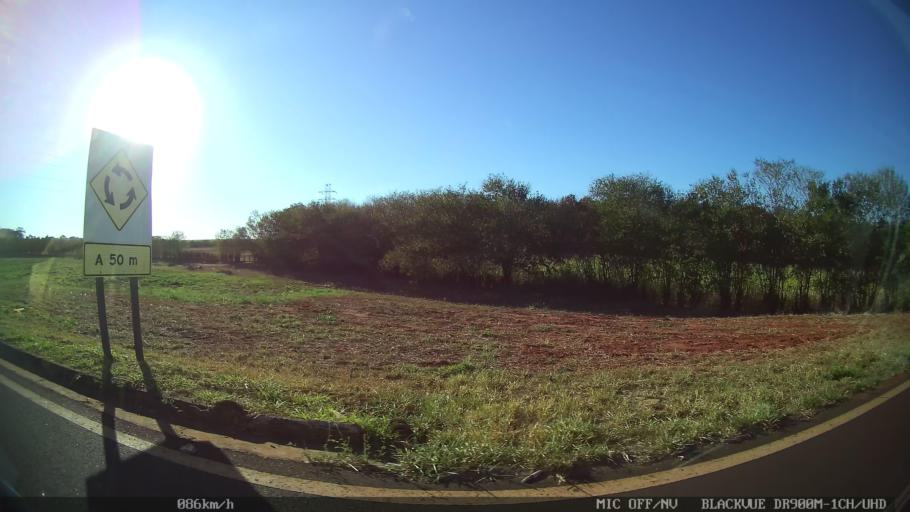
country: BR
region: Sao Paulo
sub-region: Guapiacu
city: Guapiacu
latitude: -20.7719
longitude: -49.2230
